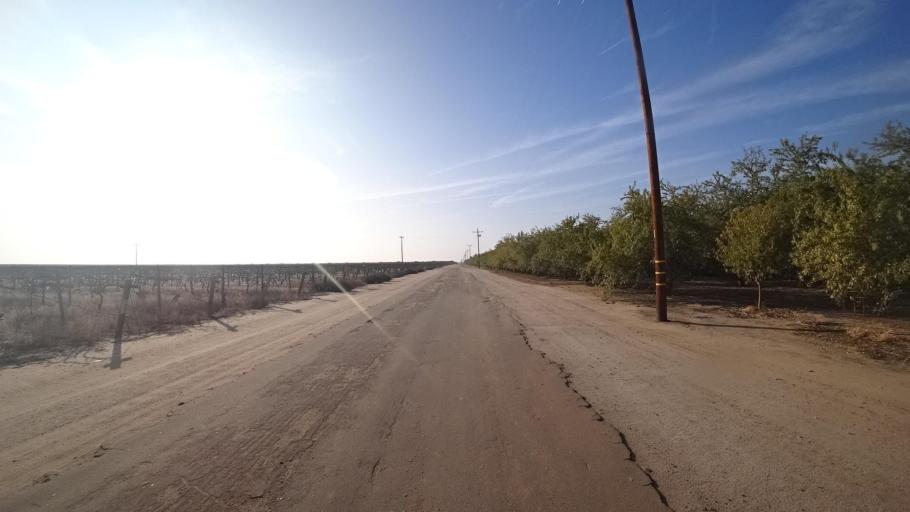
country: US
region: California
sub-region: Kern County
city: Delano
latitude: 35.7372
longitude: -119.1873
